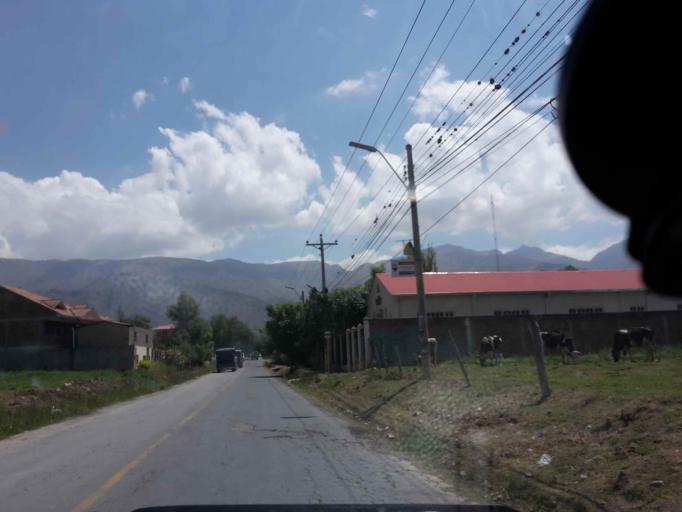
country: BO
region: Cochabamba
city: Cochabamba
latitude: -17.3536
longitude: -66.2265
